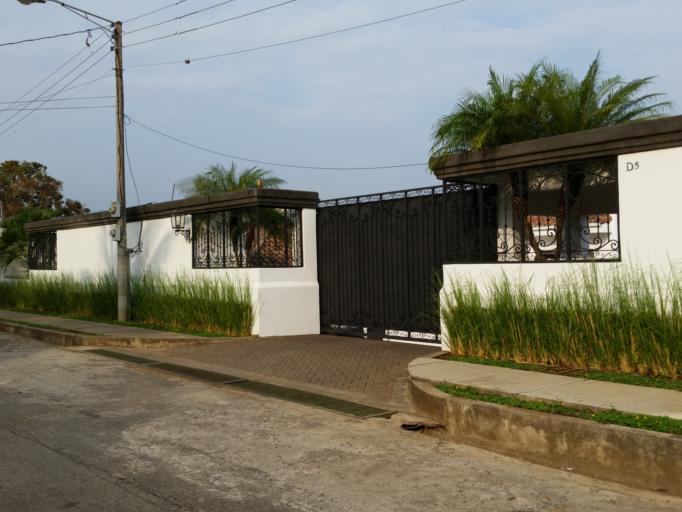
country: NI
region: Managua
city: Managua
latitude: 12.0897
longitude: -86.2483
